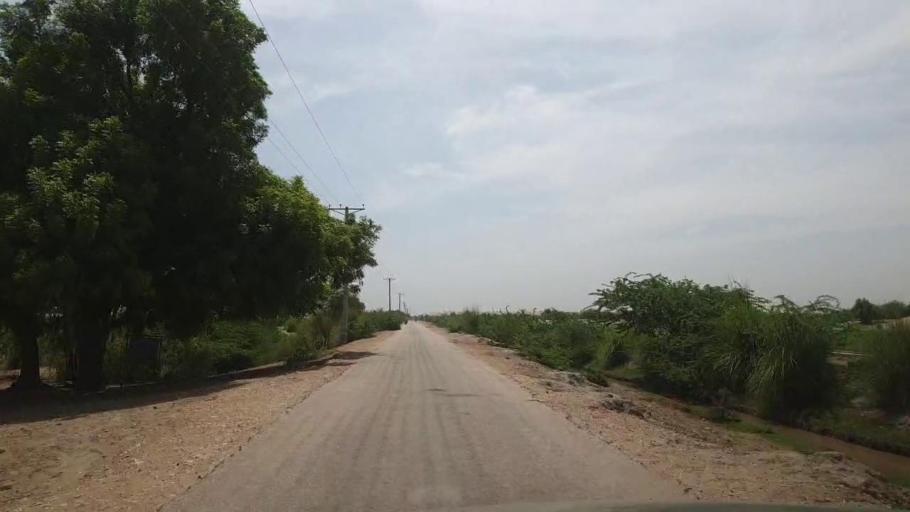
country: PK
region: Sindh
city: Kot Diji
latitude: 27.1176
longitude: 69.0080
